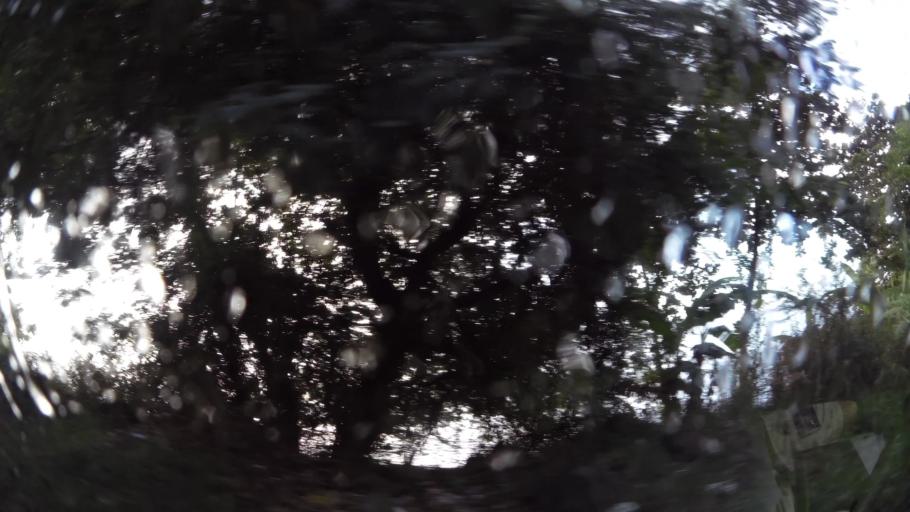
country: DM
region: Saint Paul
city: Mahaut
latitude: 15.3704
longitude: -61.4046
